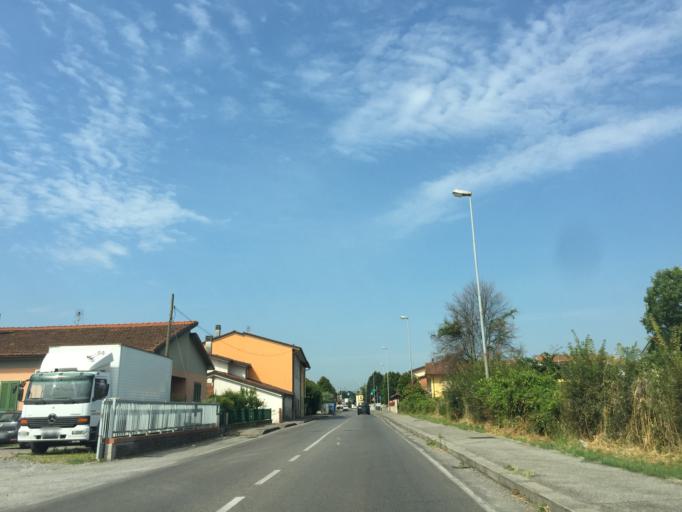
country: IT
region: Tuscany
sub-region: Provincia di Pistoia
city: Borgo a Buggiano
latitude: 43.8665
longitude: 10.7438
